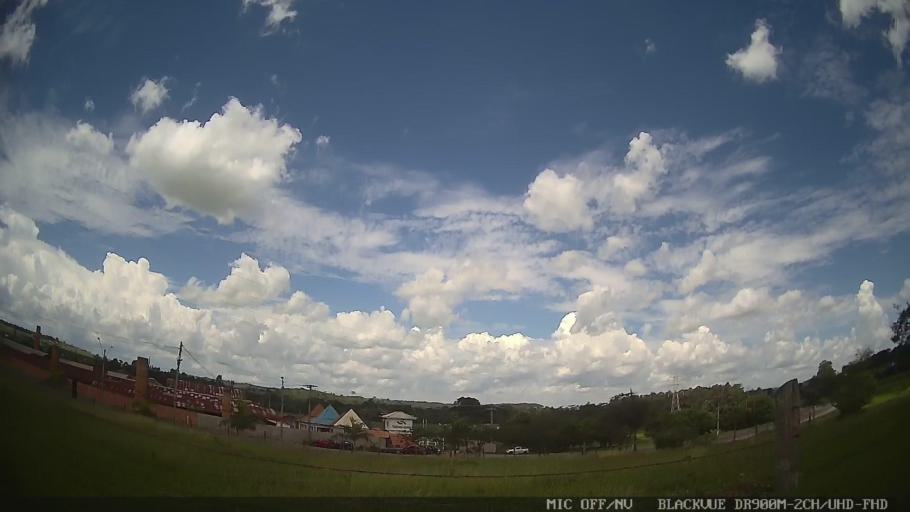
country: BR
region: Sao Paulo
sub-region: Conchas
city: Conchas
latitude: -23.0240
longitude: -47.9971
